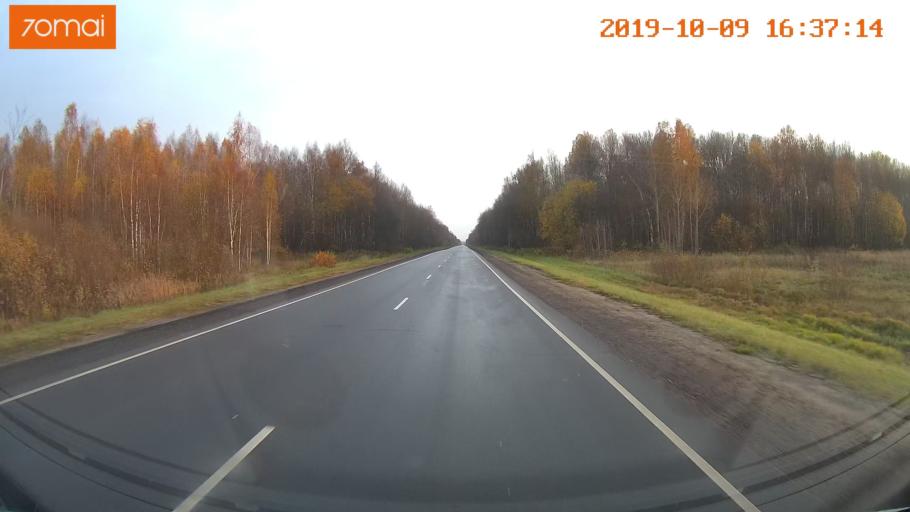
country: RU
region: Kostroma
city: Volgorechensk
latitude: 57.5301
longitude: 41.0221
